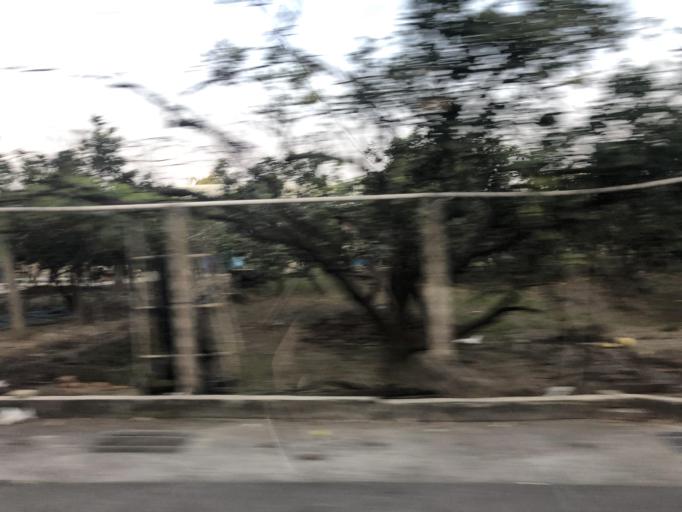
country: TW
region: Taiwan
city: Xinying
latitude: 23.1885
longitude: 120.2534
